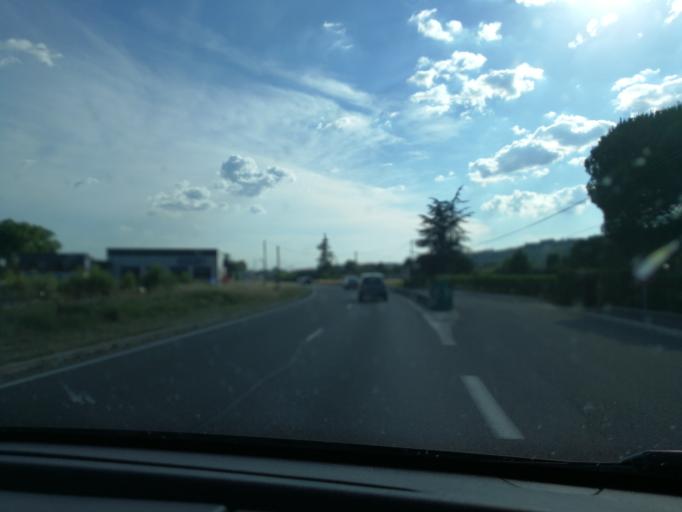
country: FR
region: Midi-Pyrenees
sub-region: Departement du Tarn
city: Cagnac-les-Mines
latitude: 43.9613
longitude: 2.1668
